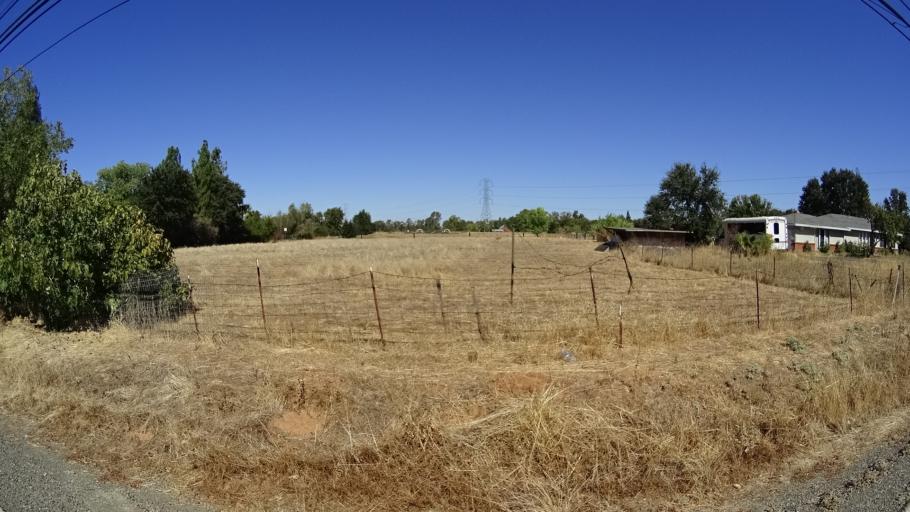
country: US
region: California
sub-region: Sacramento County
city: Vineyard
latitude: 38.4381
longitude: -121.3268
